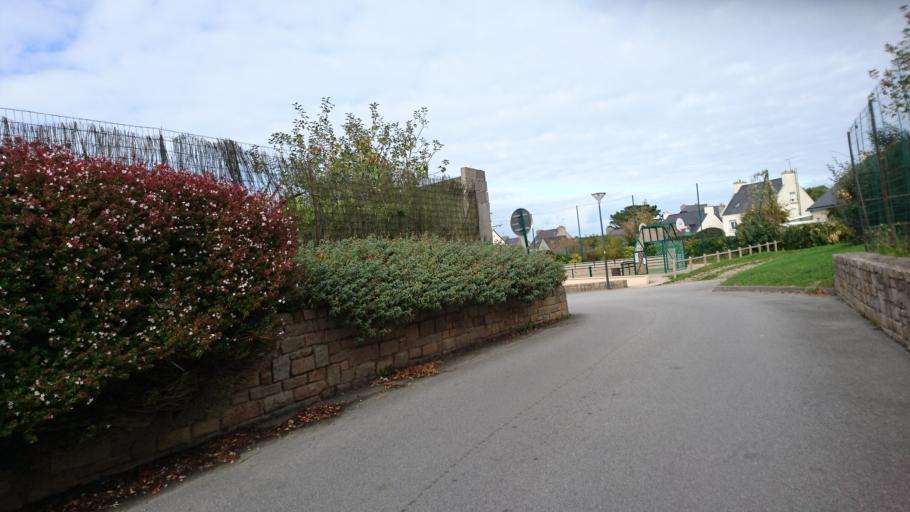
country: FR
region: Brittany
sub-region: Departement du Finistere
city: Lampaul-Plouarzel
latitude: 48.4469
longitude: -4.7612
